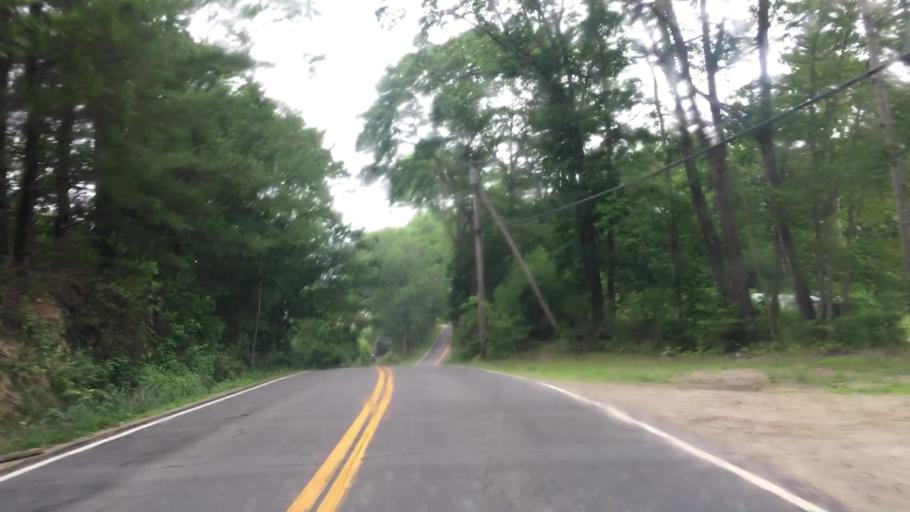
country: US
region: Maine
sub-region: Lincoln County
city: Wiscasset
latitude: 43.9884
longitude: -69.6476
